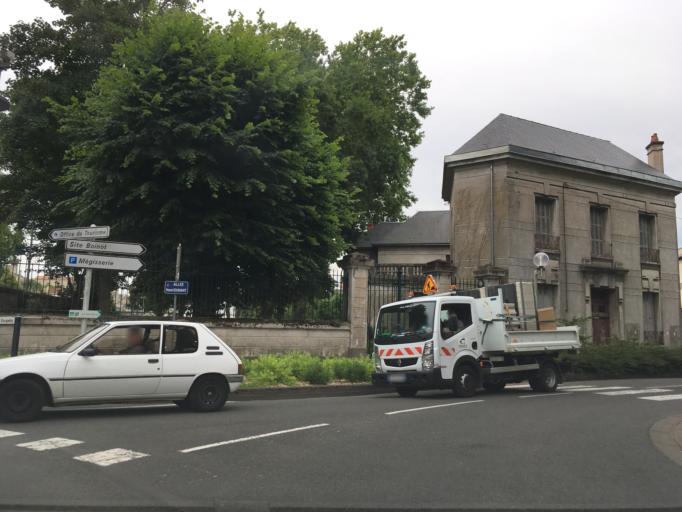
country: FR
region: Poitou-Charentes
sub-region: Departement des Deux-Sevres
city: Niort
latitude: 46.3257
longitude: -0.4685
